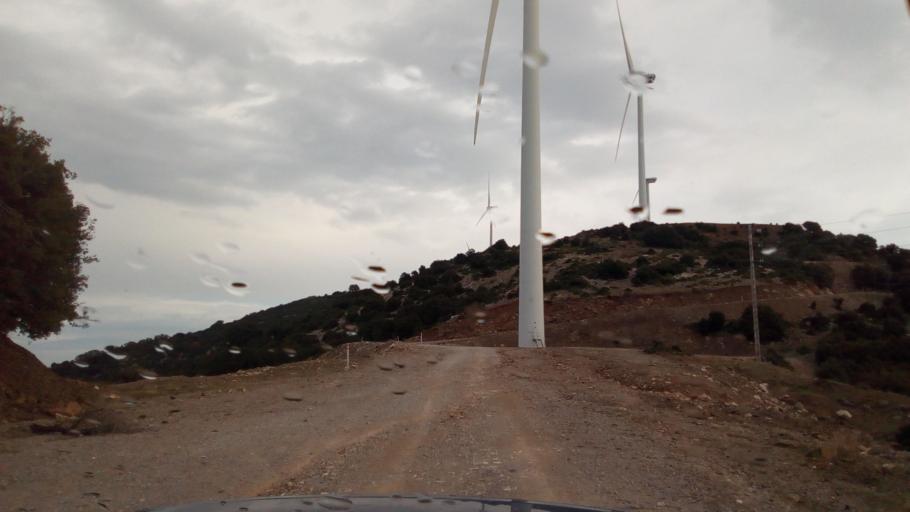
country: GR
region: West Greece
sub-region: Nomos Achaias
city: Kamarai
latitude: 38.4249
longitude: 22.0400
